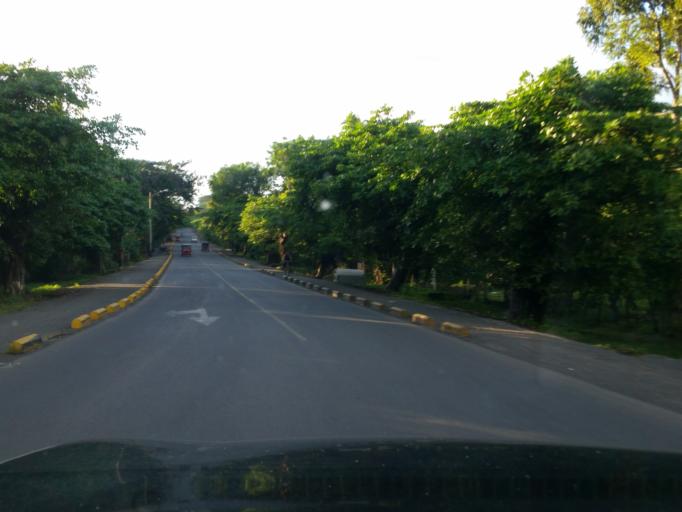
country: NI
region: Granada
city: Diriomo
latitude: 11.8531
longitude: -86.0219
